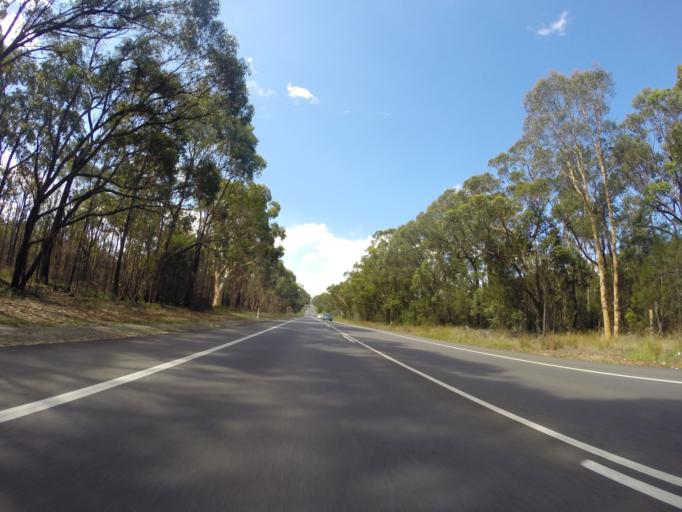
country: AU
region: New South Wales
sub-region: Shoalhaven Shire
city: Falls Creek
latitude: -35.0083
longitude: 150.5818
